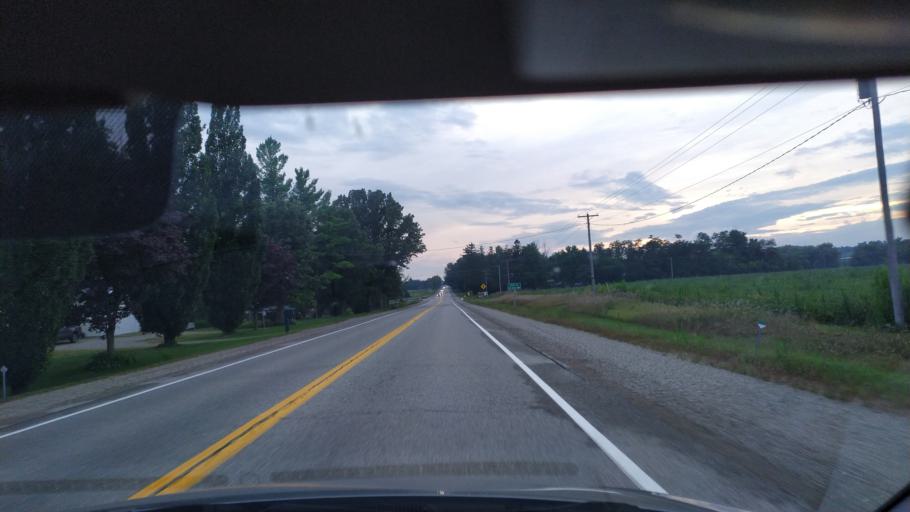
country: CA
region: Ontario
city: Kitchener
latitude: 43.3171
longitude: -80.5340
